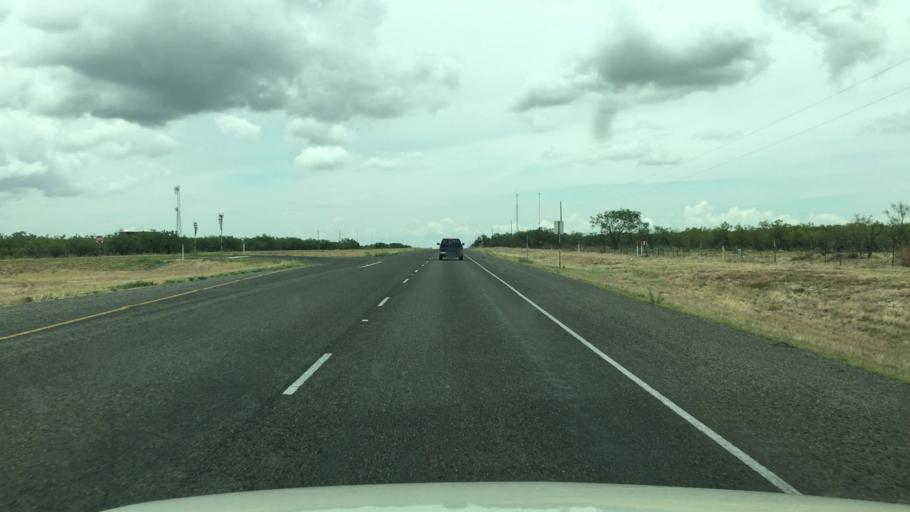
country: US
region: Texas
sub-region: Concho County
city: Eden
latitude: 31.2197
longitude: -99.9668
